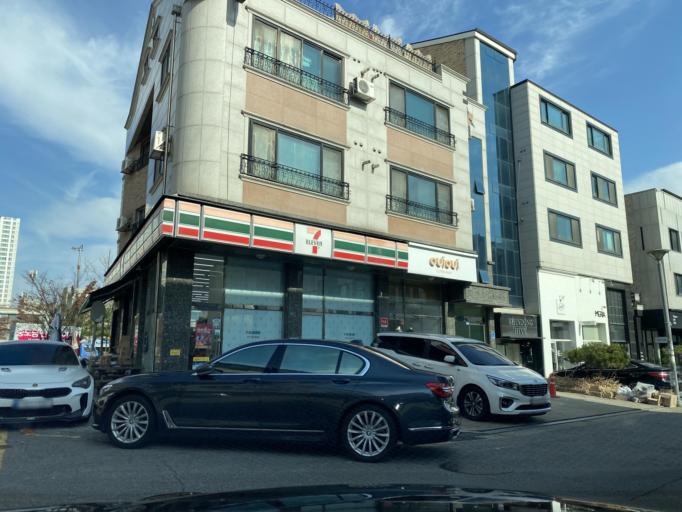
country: KR
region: Chungcheongnam-do
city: Cheonan
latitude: 36.8011
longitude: 127.1060
